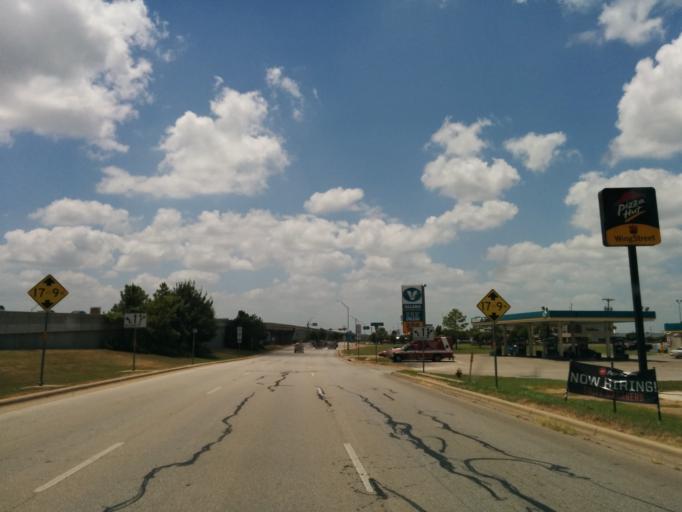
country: US
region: Texas
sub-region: Bastrop County
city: Bastrop
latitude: 30.1052
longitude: -97.3266
